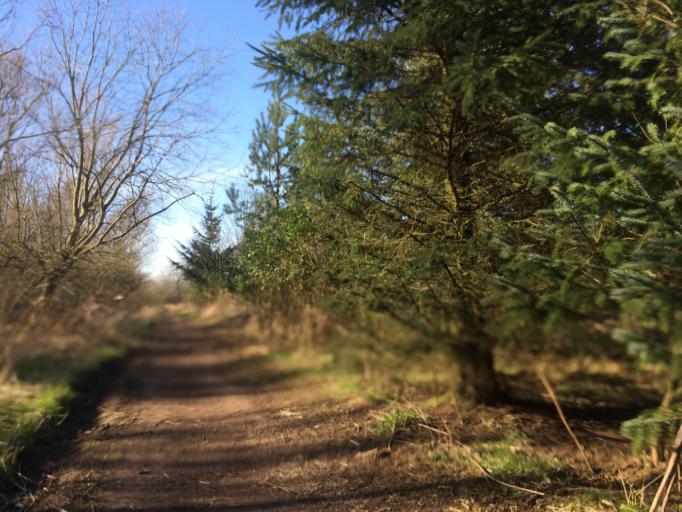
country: GB
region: Scotland
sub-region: Fife
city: Thornton
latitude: 56.1716
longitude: -3.1478
